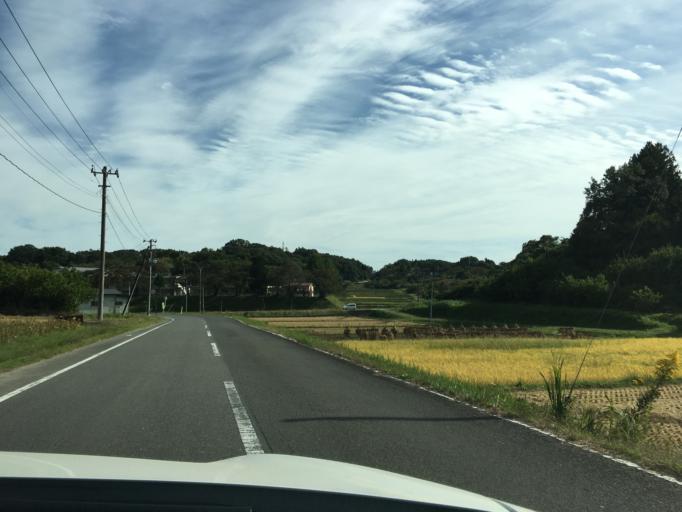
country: JP
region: Fukushima
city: Nihommatsu
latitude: 37.5800
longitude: 140.4716
